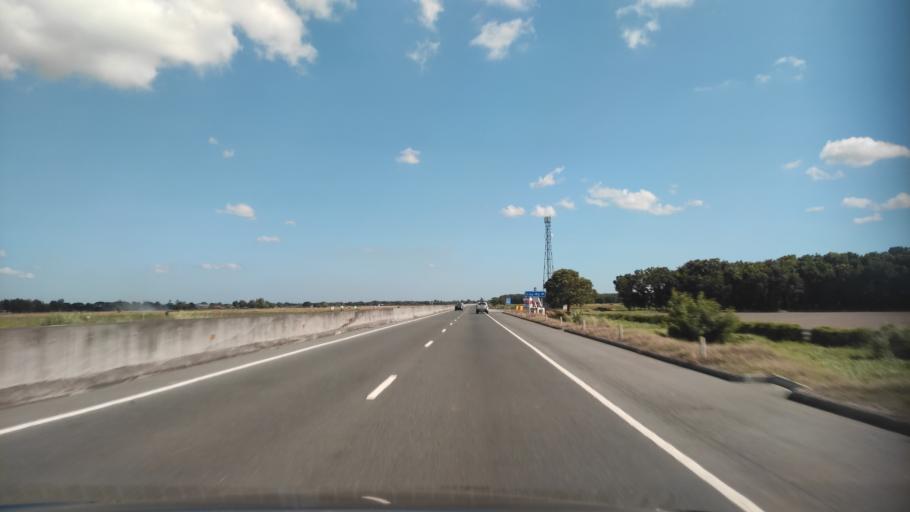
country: PH
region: Central Luzon
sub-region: Province of Tarlac
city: Balite
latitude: 15.6412
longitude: 120.6235
